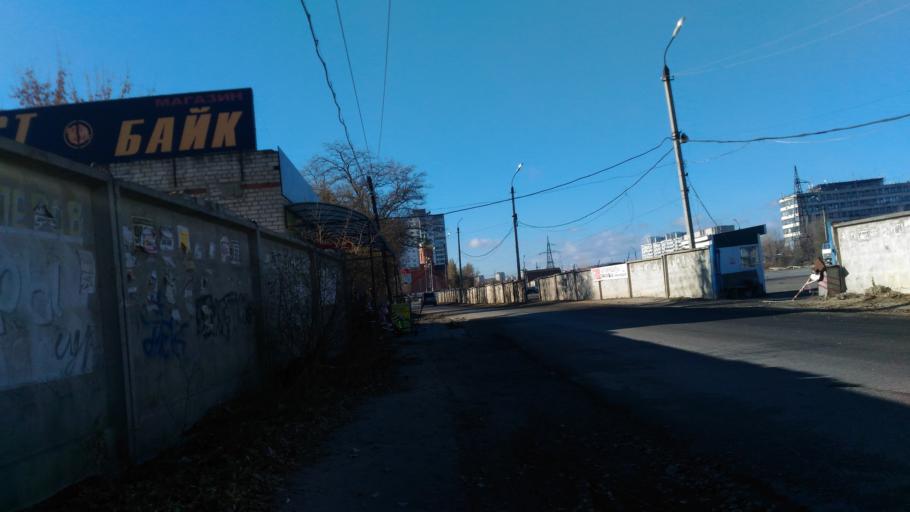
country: RU
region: Volgograd
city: Volgograd
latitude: 48.6544
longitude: 44.4404
